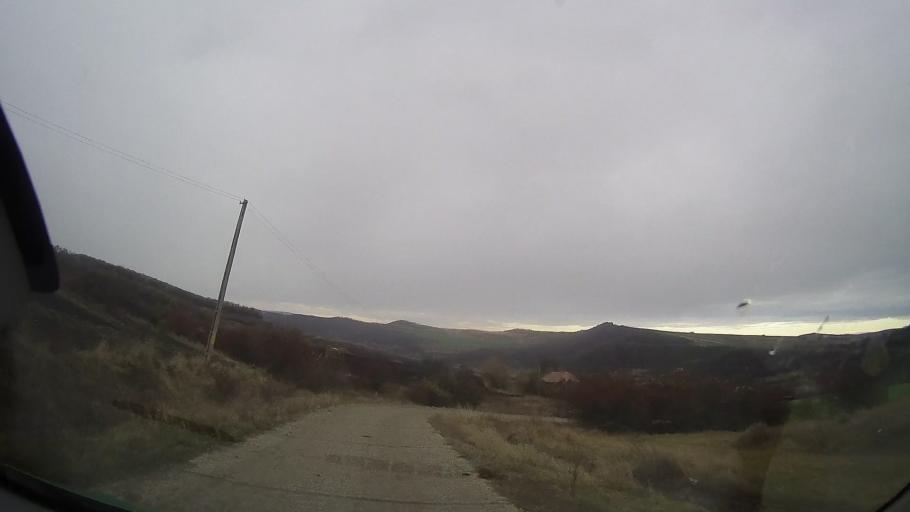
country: RO
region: Mures
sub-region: Comuna Bala
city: Bala
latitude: 46.6756
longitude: 24.4839
